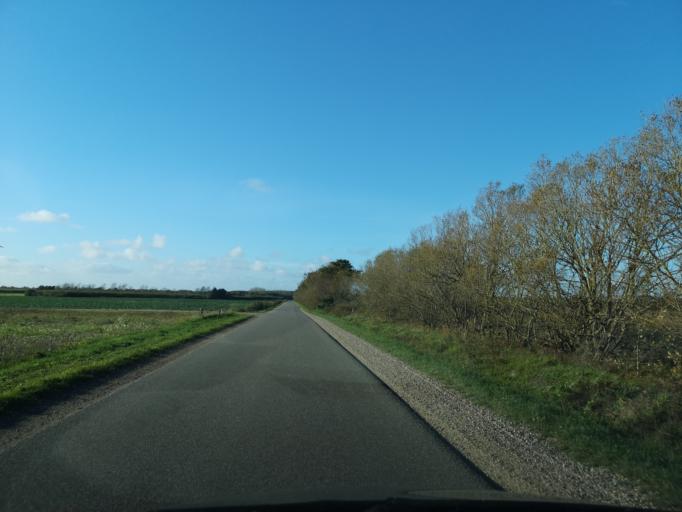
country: DK
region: Central Jutland
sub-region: Ringkobing-Skjern Kommune
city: Tarm
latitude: 55.8122
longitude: 8.4362
